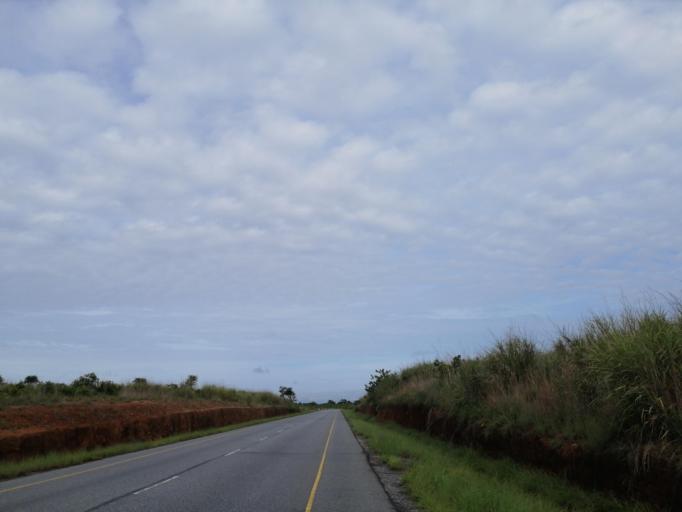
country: SL
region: Northern Province
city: Port Loko
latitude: 8.7836
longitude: -12.8522
